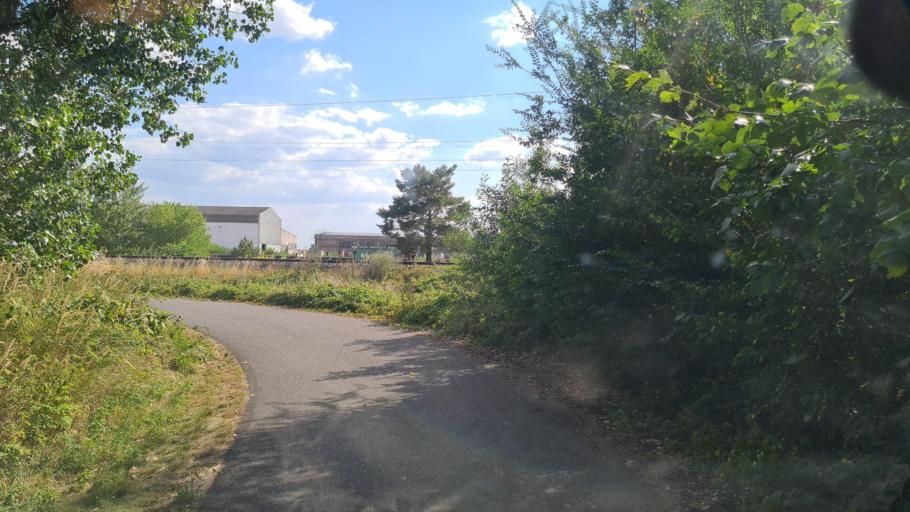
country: DE
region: Saxony-Anhalt
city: Elster
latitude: 51.8381
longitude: 12.8093
